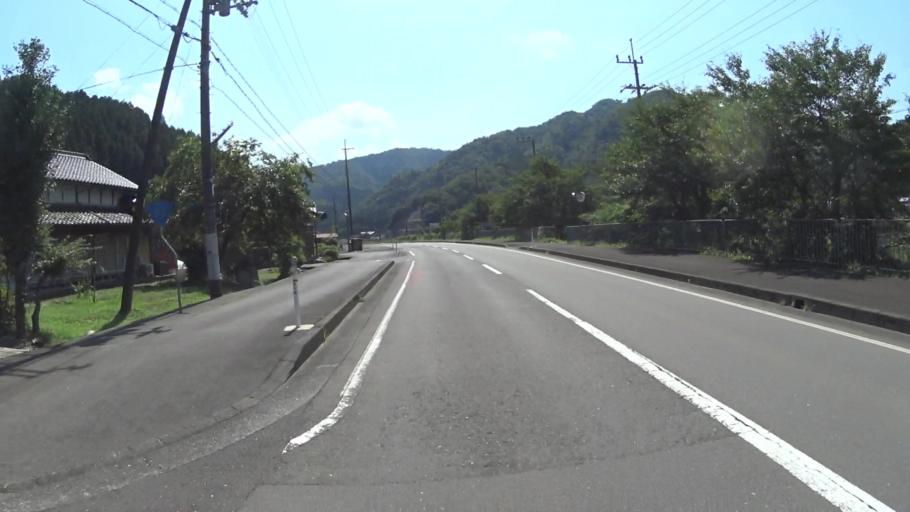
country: JP
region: Fukui
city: Obama
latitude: 35.4213
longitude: 135.6857
